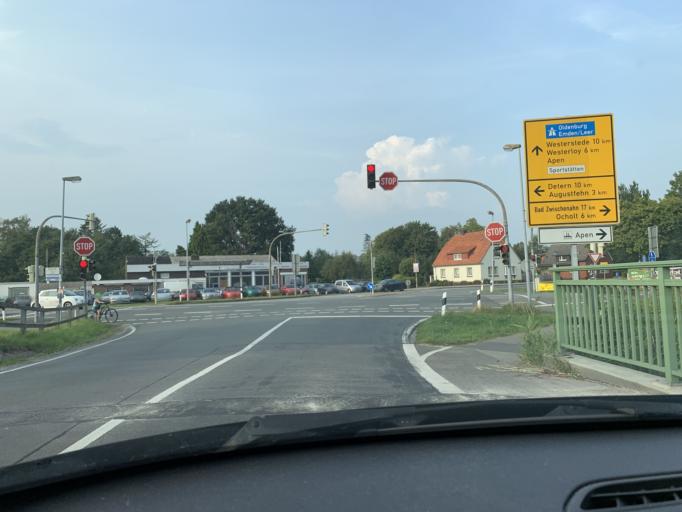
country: DE
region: Lower Saxony
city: Apen
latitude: 53.2169
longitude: 7.7974
